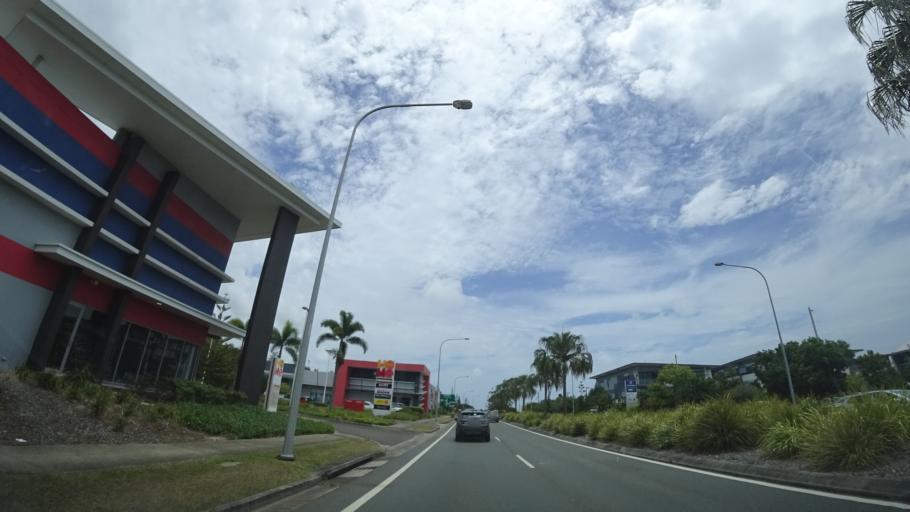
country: AU
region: Queensland
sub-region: Sunshine Coast
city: Mooloolaba
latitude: -26.7339
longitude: 153.1204
